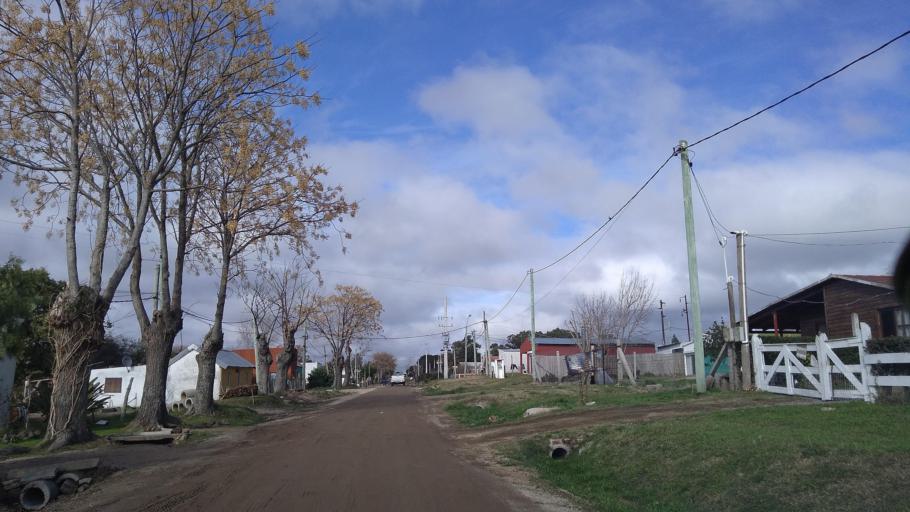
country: UY
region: Canelones
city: Tala
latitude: -34.1908
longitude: -55.7419
